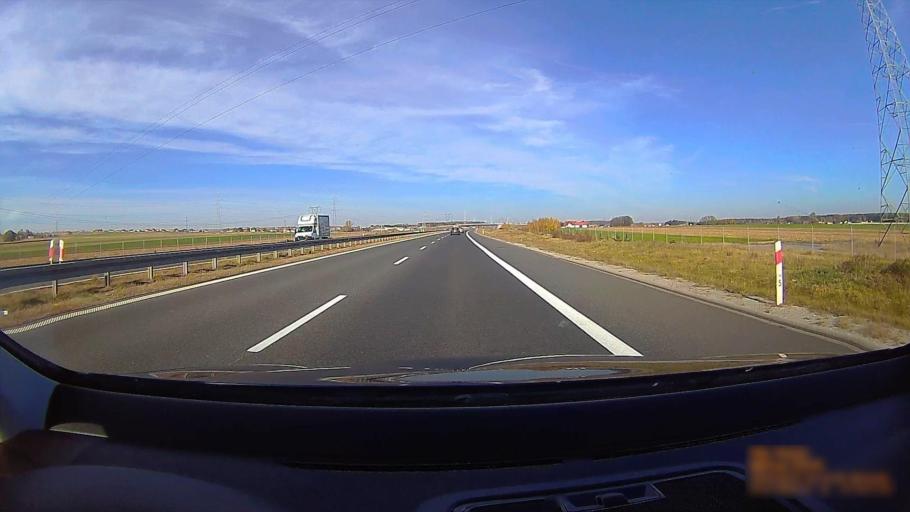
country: PL
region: Greater Poland Voivodeship
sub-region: Powiat ostrowski
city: Przygodzice
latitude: 51.5937
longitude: 17.8505
